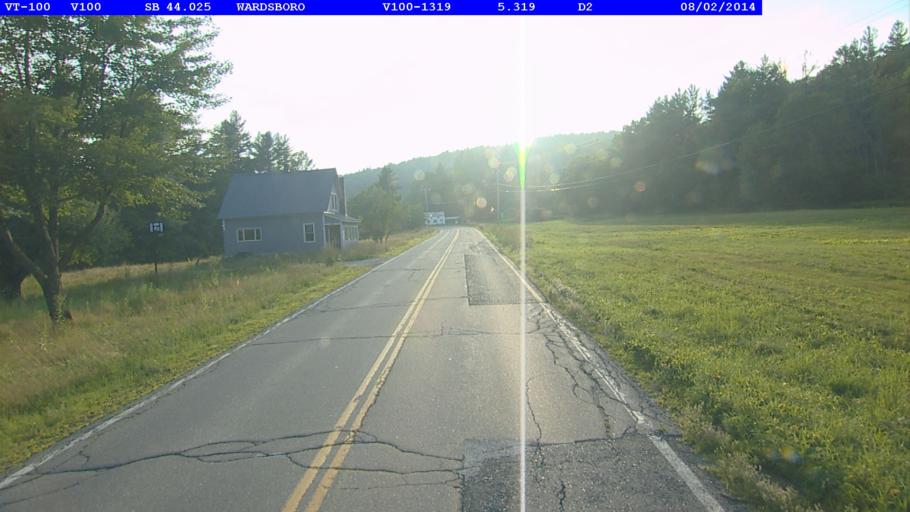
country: US
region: Vermont
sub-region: Windham County
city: Dover
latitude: 43.0347
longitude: -72.8079
